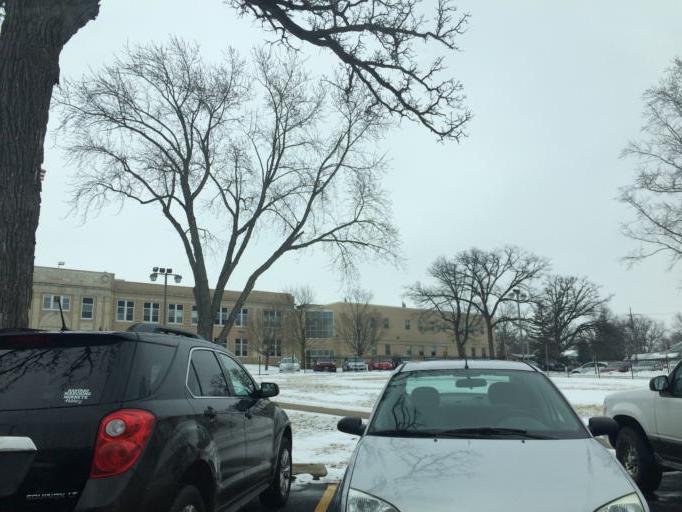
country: US
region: Illinois
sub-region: McHenry County
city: Harvard
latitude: 42.4285
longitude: -88.6109
